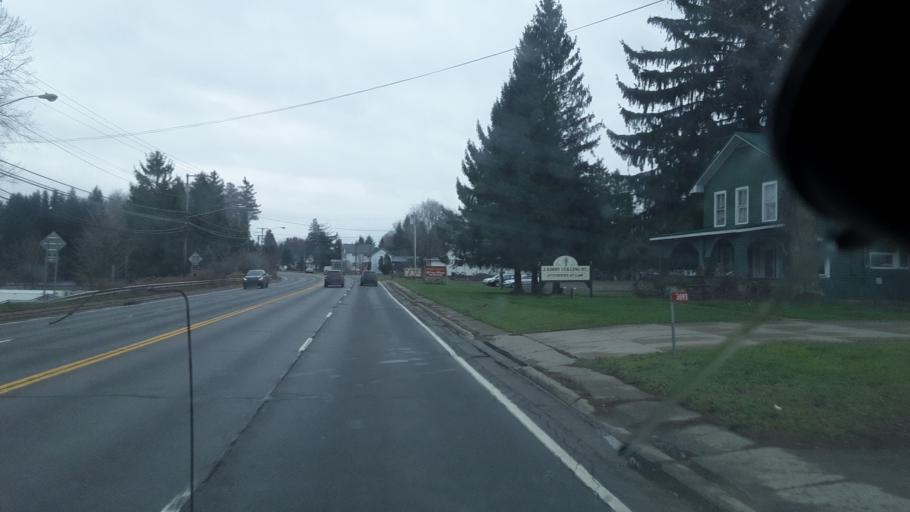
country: US
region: New York
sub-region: Cattaraugus County
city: Yorkshire
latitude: 42.5301
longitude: -78.4699
